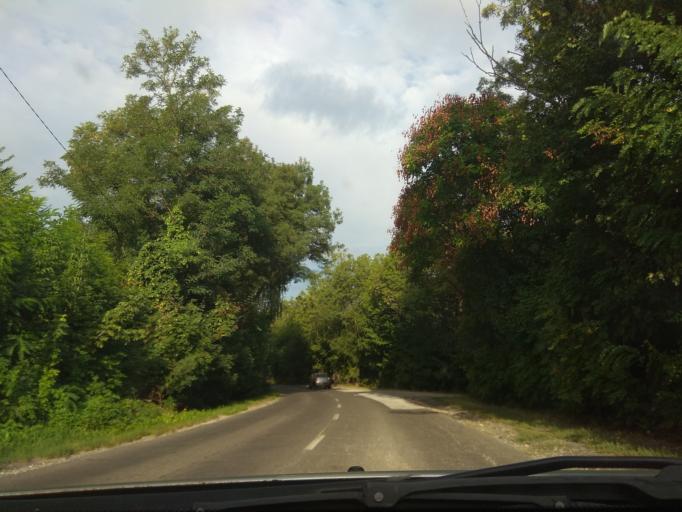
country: HU
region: Borsod-Abauj-Zemplen
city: Miskolc
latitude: 48.0884
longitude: 20.7340
